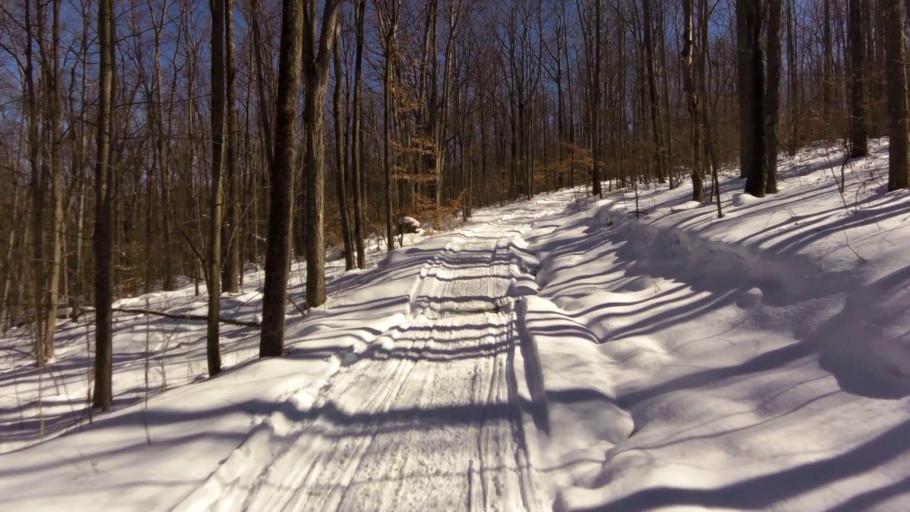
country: US
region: New York
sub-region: Allegany County
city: Houghton
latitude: 42.3632
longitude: -78.1905
